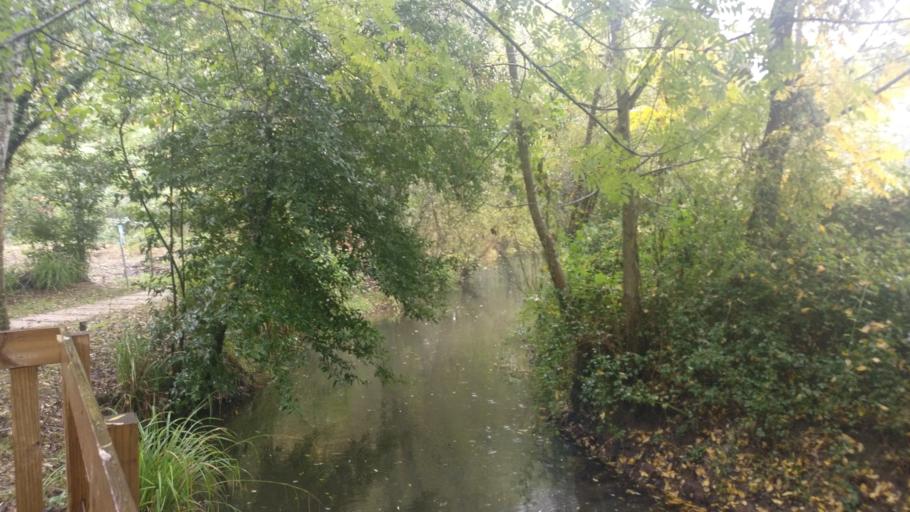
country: PT
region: Viseu
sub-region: Mortagua
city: Mortagua
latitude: 40.3947
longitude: -8.2274
